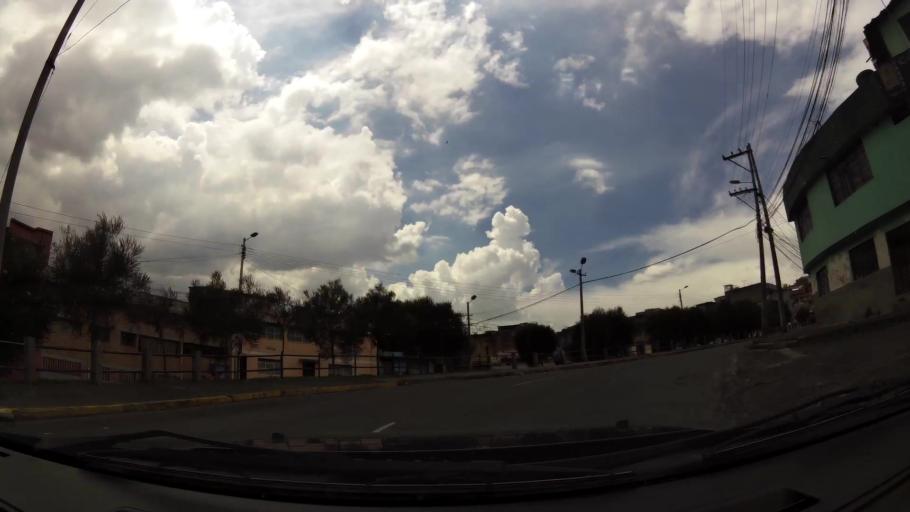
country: EC
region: Pichincha
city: Quito
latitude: -0.2516
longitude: -78.5139
